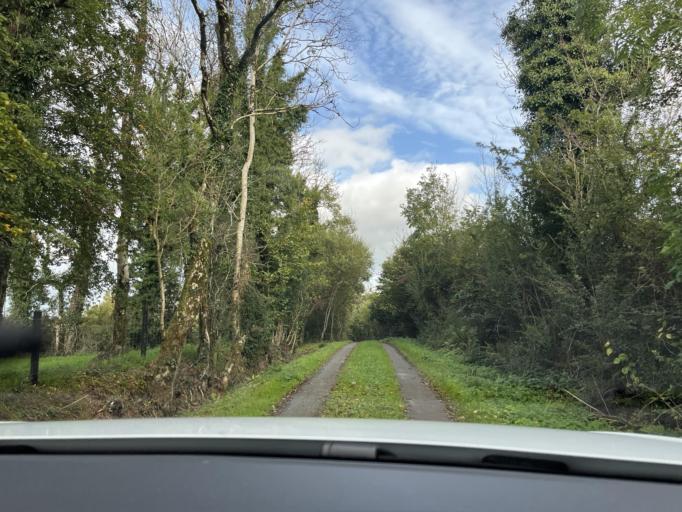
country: IE
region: Connaught
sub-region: County Leitrim
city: Carrick-on-Shannon
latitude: 53.9739
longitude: -8.0732
